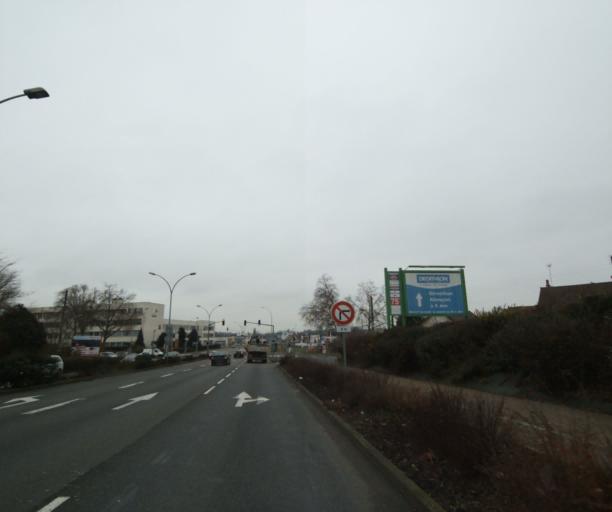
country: FR
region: Pays de la Loire
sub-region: Departement de la Sarthe
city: Le Mans
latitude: 47.9838
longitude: 0.1867
